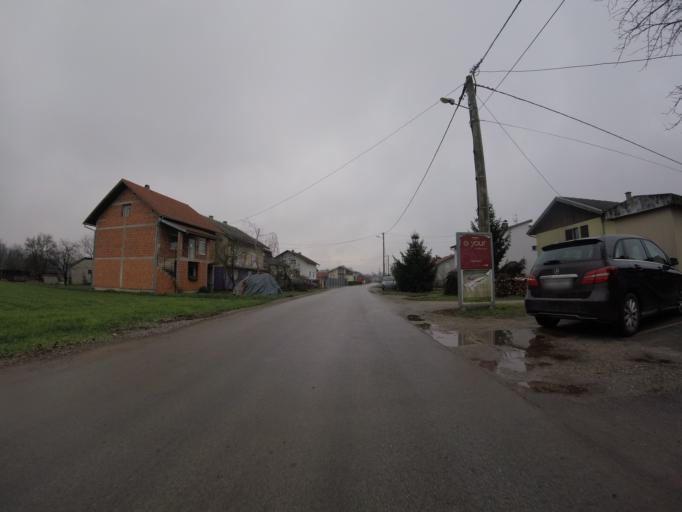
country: HR
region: Zagrebacka
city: Kuce
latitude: 45.7071
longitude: 16.1215
